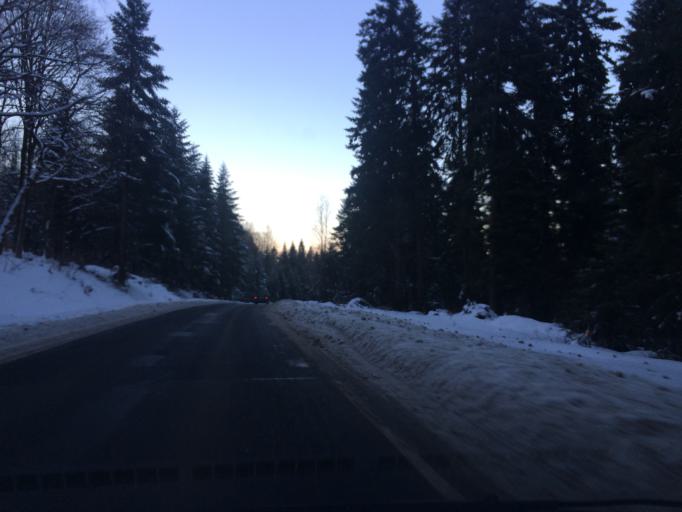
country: PL
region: Subcarpathian Voivodeship
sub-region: Powiat bieszczadzki
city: Czarna
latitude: 49.2940
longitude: 22.6706
